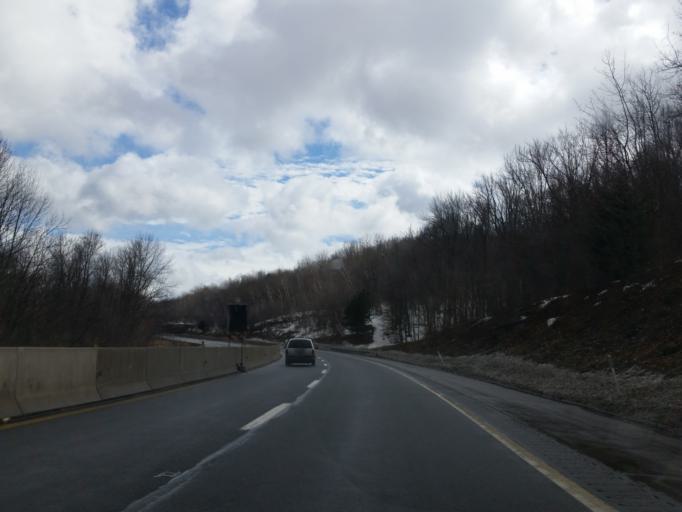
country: US
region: Pennsylvania
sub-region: Lackawanna County
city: Clarks Summit
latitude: 41.4687
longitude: -75.7034
